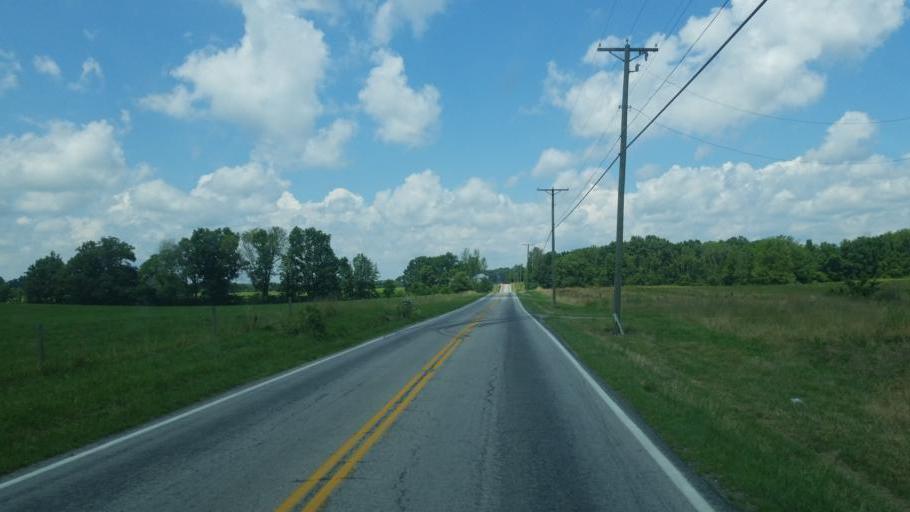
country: US
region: Ohio
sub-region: Highland County
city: Greenfield
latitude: 39.2312
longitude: -83.4271
